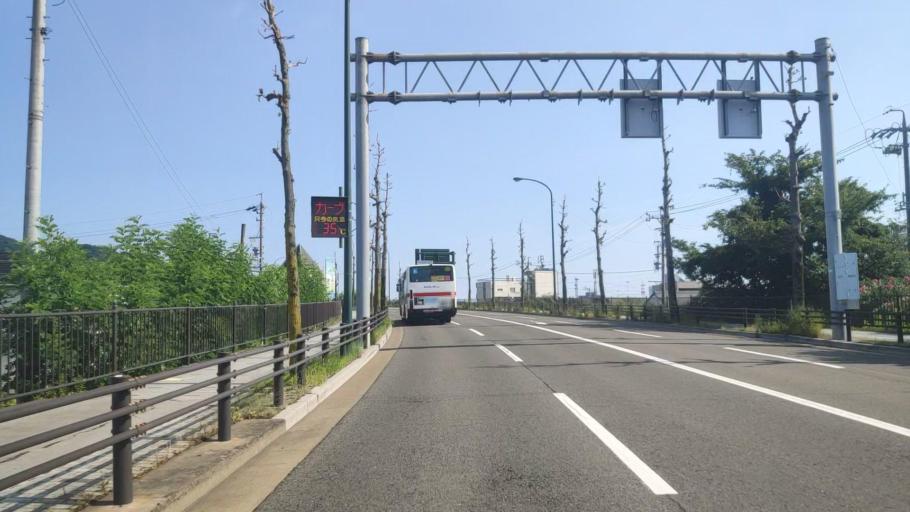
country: JP
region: Gifu
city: Gifu-shi
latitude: 35.4359
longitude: 136.7604
